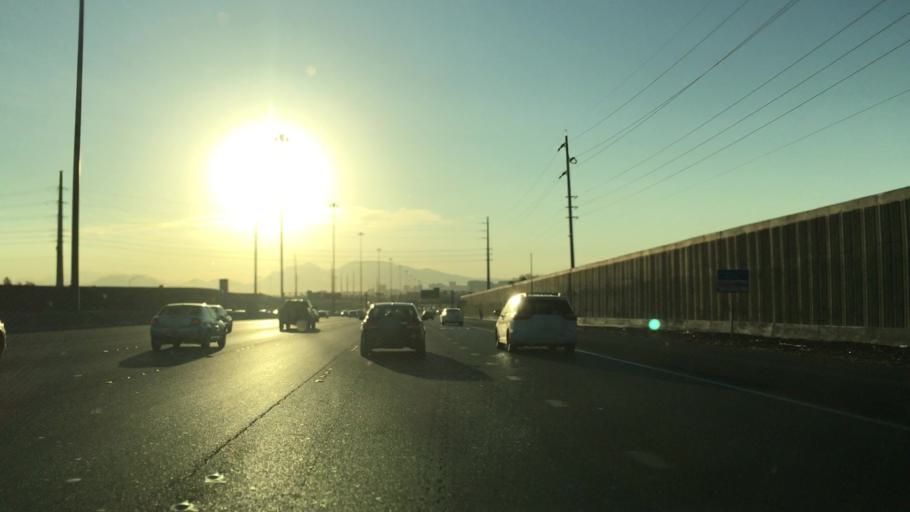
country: US
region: Nevada
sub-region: Clark County
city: Spring Valley
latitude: 36.1737
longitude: -115.2172
